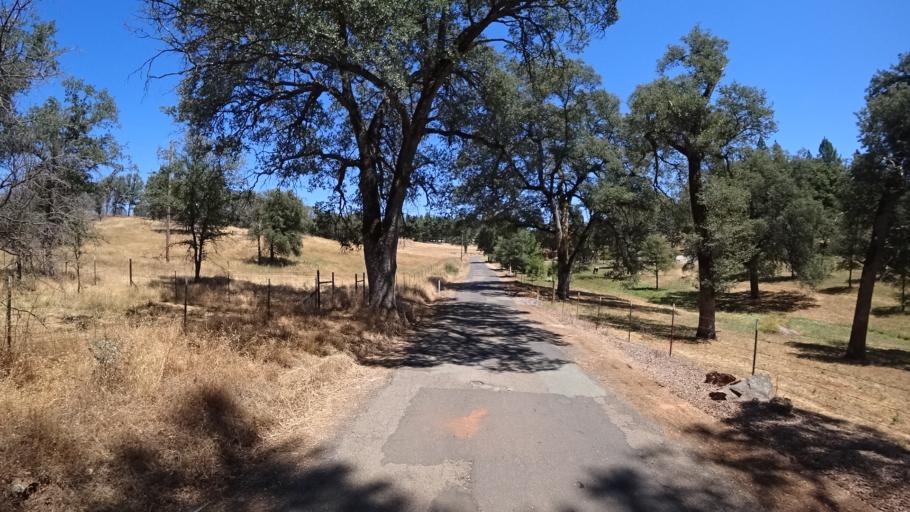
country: US
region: California
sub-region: Calaveras County
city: Mountain Ranch
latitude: 38.2904
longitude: -120.6019
